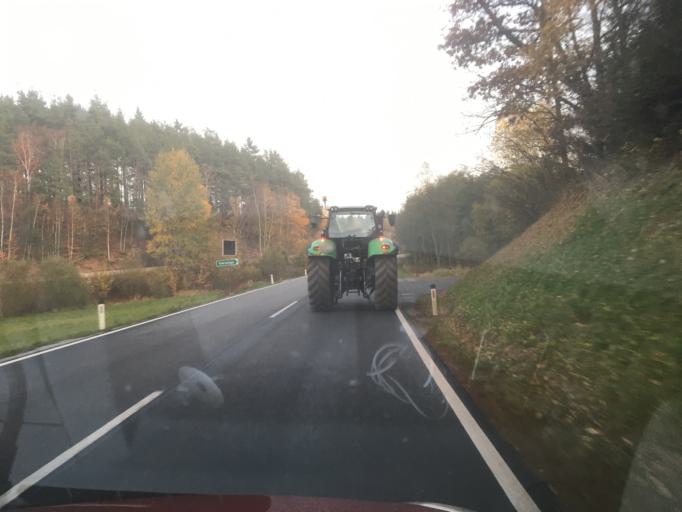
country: AT
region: Lower Austria
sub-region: Politischer Bezirk Zwettl
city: Langschlag
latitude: 48.5751
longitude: 14.8972
